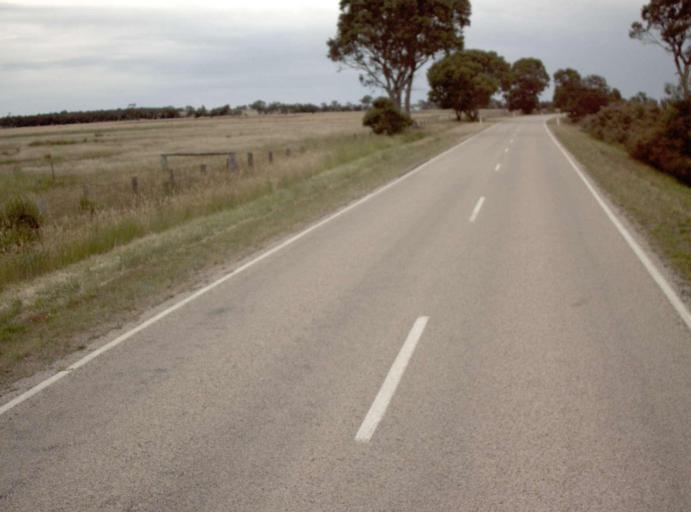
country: AU
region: Victoria
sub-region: East Gippsland
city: Bairnsdale
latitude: -37.8908
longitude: 147.5566
